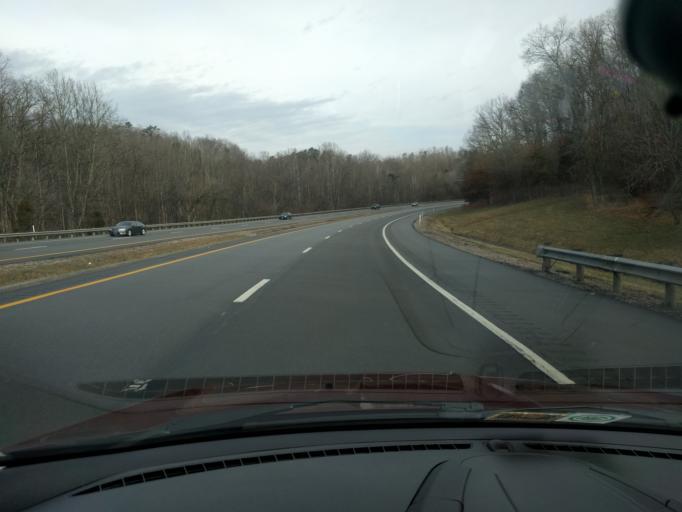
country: US
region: West Virginia
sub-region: Jackson County
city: Ripley
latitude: 38.7948
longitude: -81.7324
